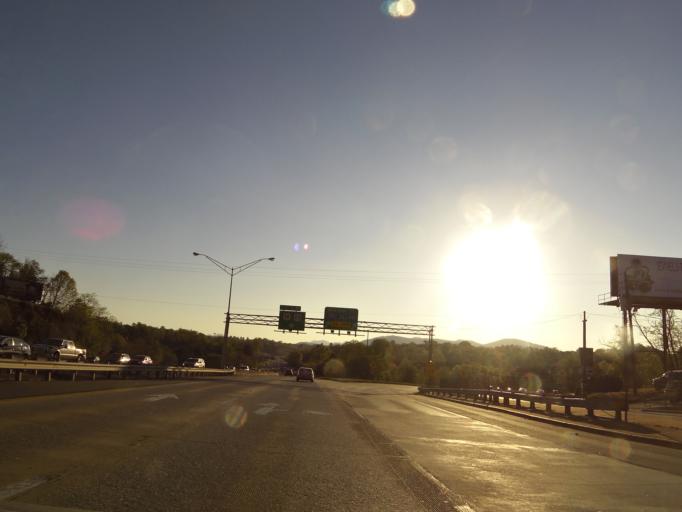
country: US
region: North Carolina
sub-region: Buncombe County
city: Asheville
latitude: 35.5899
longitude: -82.5769
